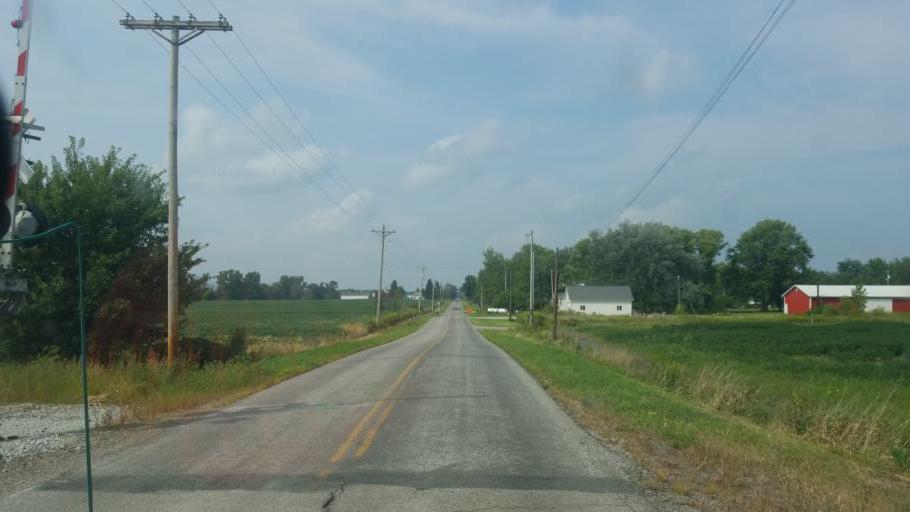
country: US
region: Ohio
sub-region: Lorain County
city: Wellington
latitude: 41.1247
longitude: -82.1609
